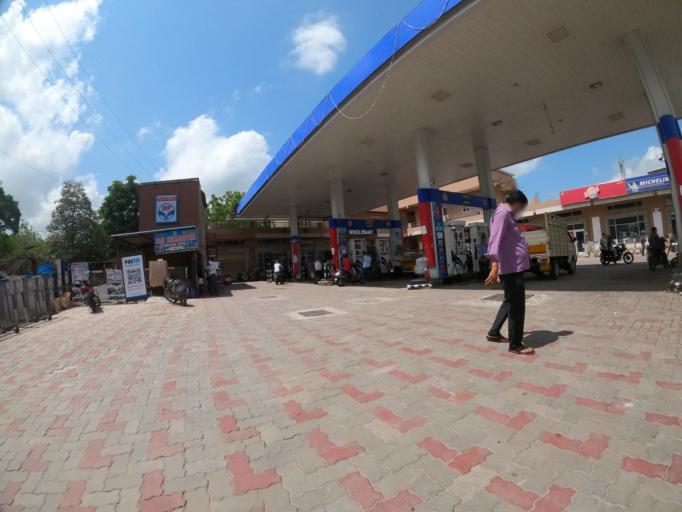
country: IN
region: Telangana
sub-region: Hyderabad
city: Hyderabad
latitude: 17.3592
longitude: 78.3878
